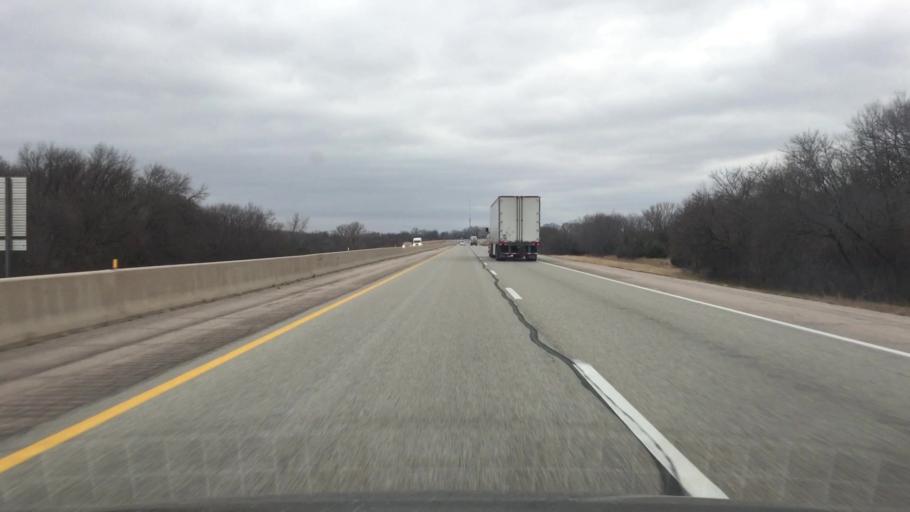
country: US
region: Kansas
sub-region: Butler County
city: El Dorado
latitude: 37.8636
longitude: -96.8587
